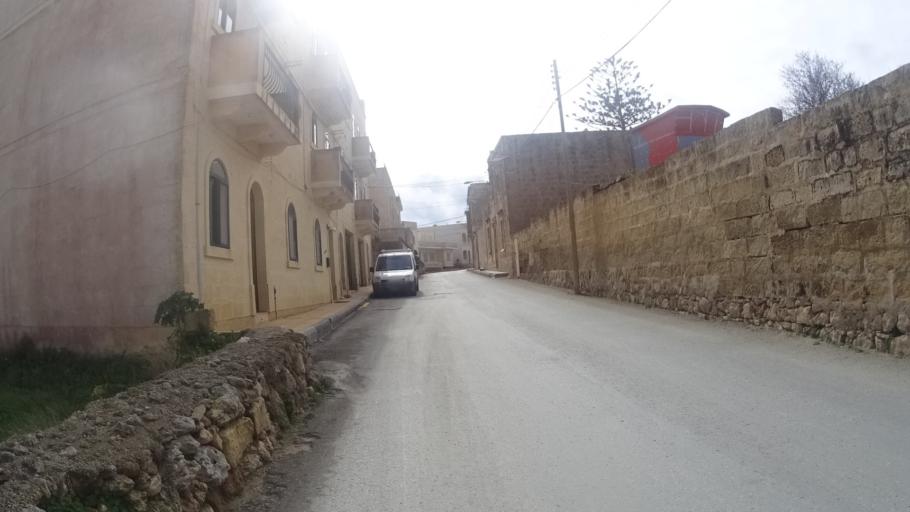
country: MT
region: In-Nadur
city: Nadur
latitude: 36.0429
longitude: 14.2983
